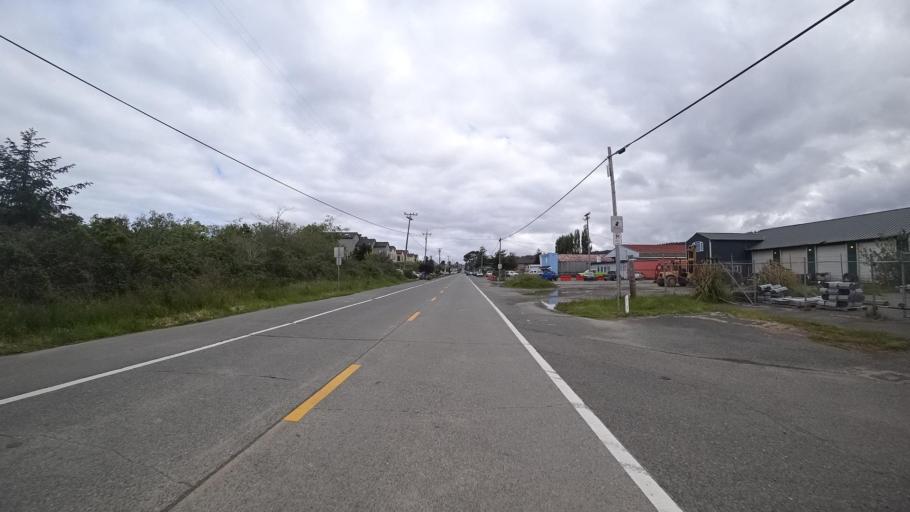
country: US
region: California
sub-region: Humboldt County
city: Arcata
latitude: 40.8599
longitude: -124.0891
